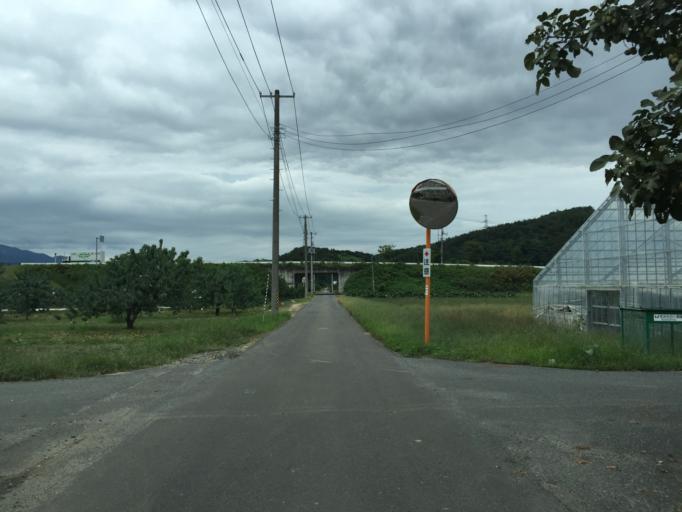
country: JP
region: Fukushima
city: Hobaramachi
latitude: 37.7963
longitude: 140.5077
